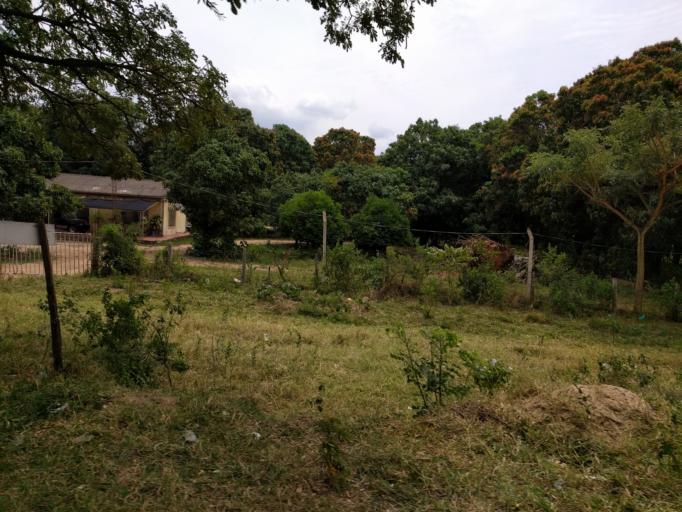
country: BO
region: Santa Cruz
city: Santa Rita
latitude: -17.9131
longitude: -63.3448
